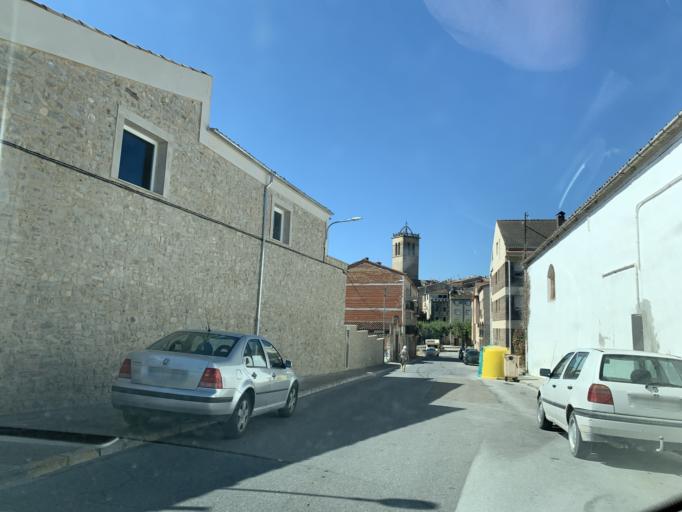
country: ES
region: Catalonia
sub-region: Provincia de Tarragona
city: Santa Coloma de Queralt
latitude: 41.5339
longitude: 1.3860
